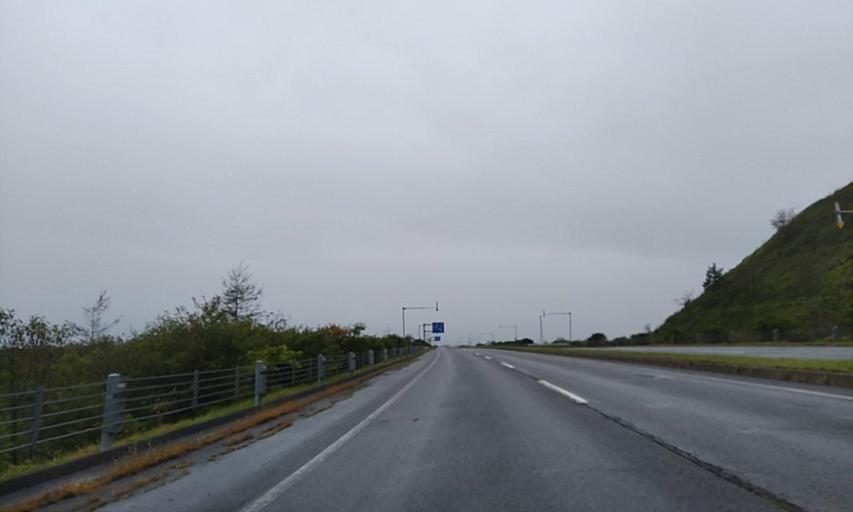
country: JP
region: Hokkaido
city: Kushiro
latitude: 43.0168
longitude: 144.2567
